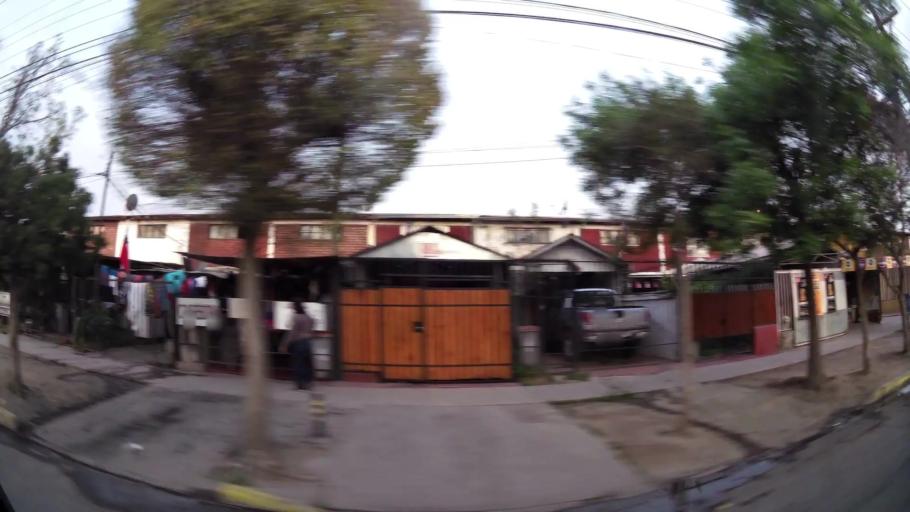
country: CL
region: Santiago Metropolitan
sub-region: Provincia de Santiago
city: Lo Prado
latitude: -33.5114
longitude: -70.7846
